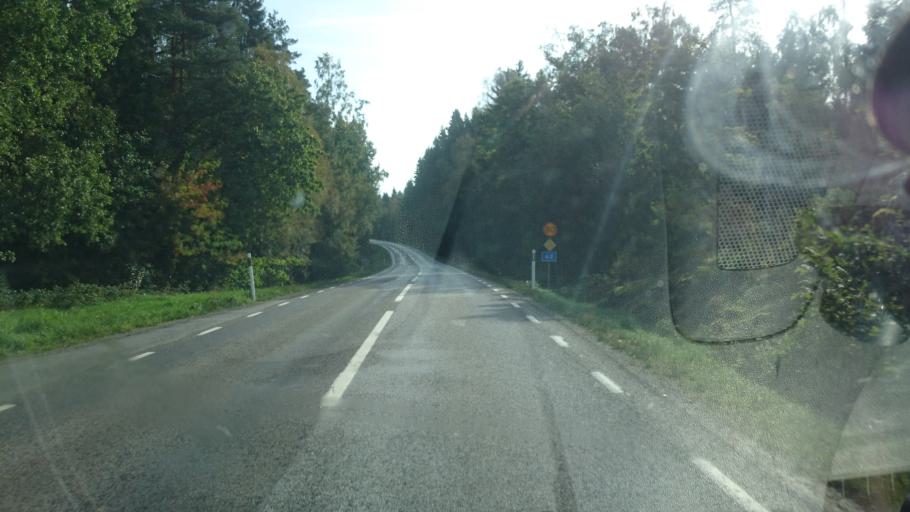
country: SE
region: Vaestra Goetaland
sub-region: Alingsas Kommun
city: Sollebrunn
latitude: 58.1316
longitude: 12.4876
